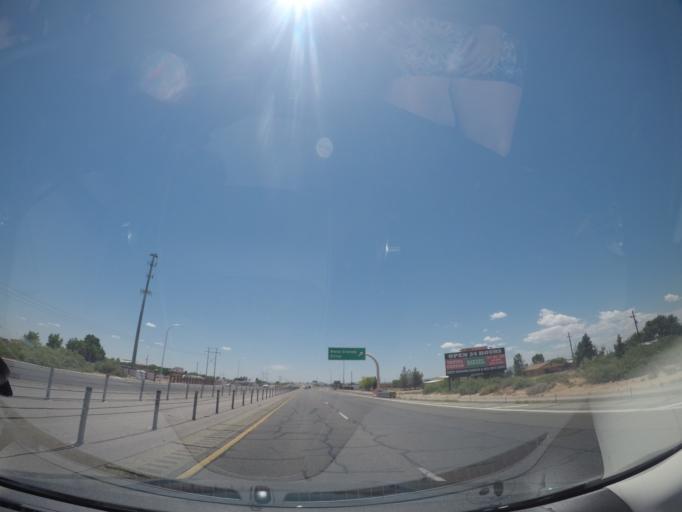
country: US
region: New Mexico
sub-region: Dona Ana County
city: Las Cruces
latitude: 32.3863
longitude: -106.7118
